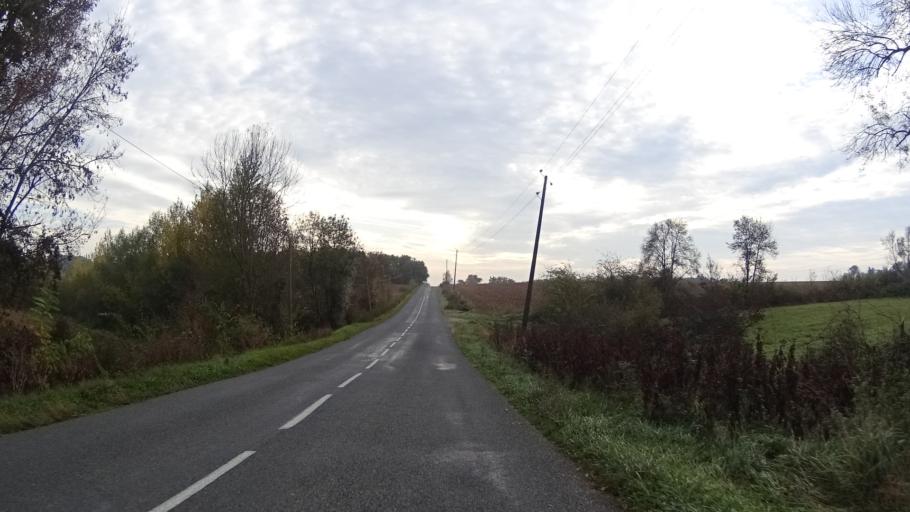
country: FR
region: Aquitaine
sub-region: Departement du Lot-et-Garonne
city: Laplume
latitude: 44.0961
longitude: 0.5680
